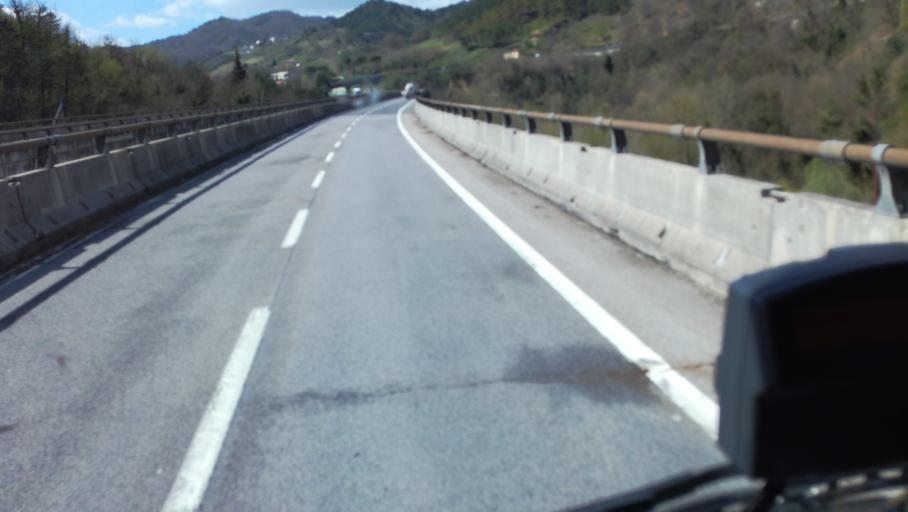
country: IT
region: Emilia-Romagna
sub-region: Forli-Cesena
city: Sarsina
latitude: 43.9143
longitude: 12.1400
